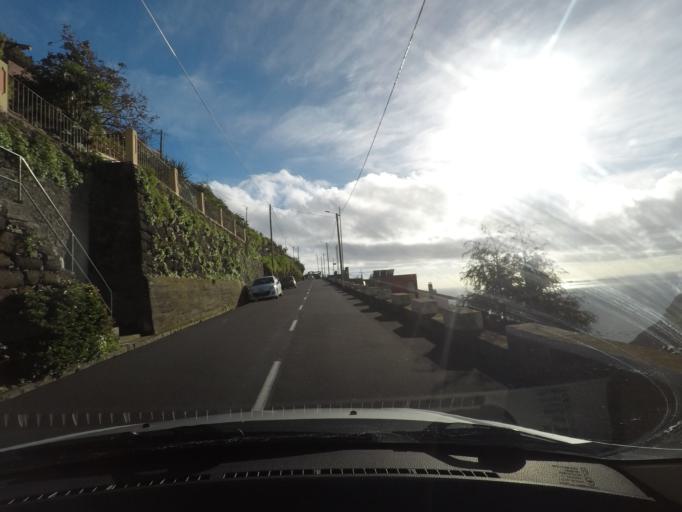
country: PT
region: Madeira
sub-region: Ribeira Brava
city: Campanario
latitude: 32.6683
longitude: -17.0375
